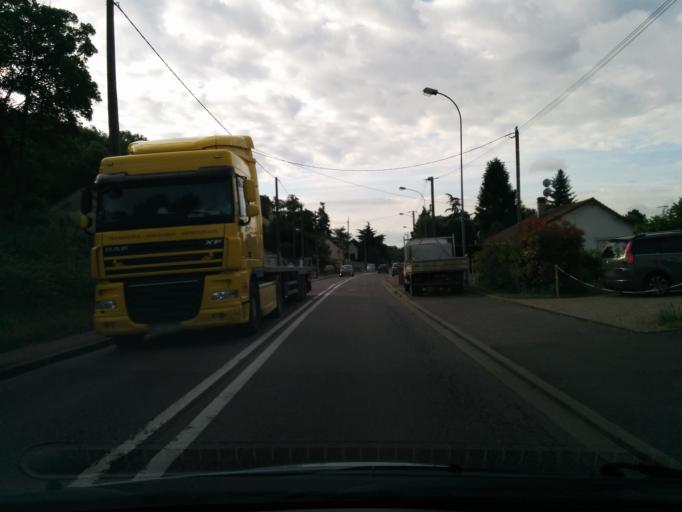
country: FR
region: Ile-de-France
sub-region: Departement des Yvelines
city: Follainville-Dennemont
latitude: 49.0044
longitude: 1.7180
